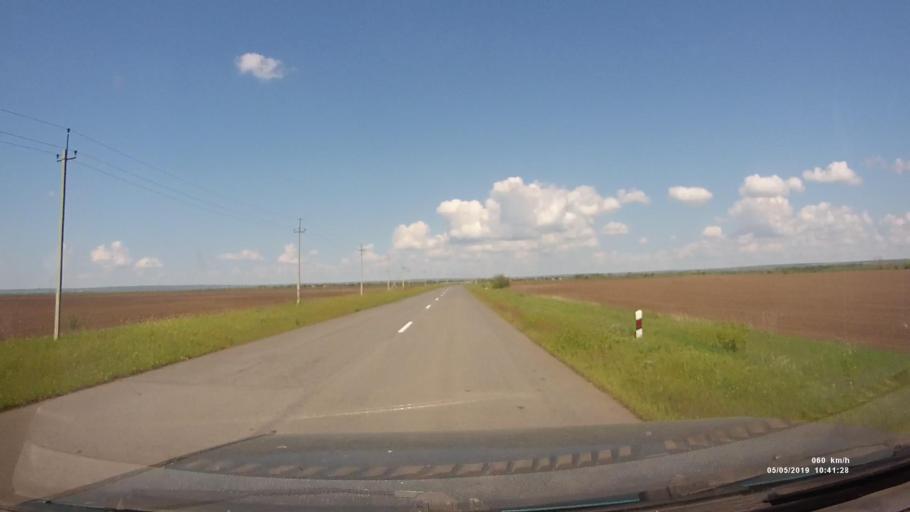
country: RU
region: Rostov
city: Ust'-Donetskiy
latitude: 47.5911
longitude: 40.8421
